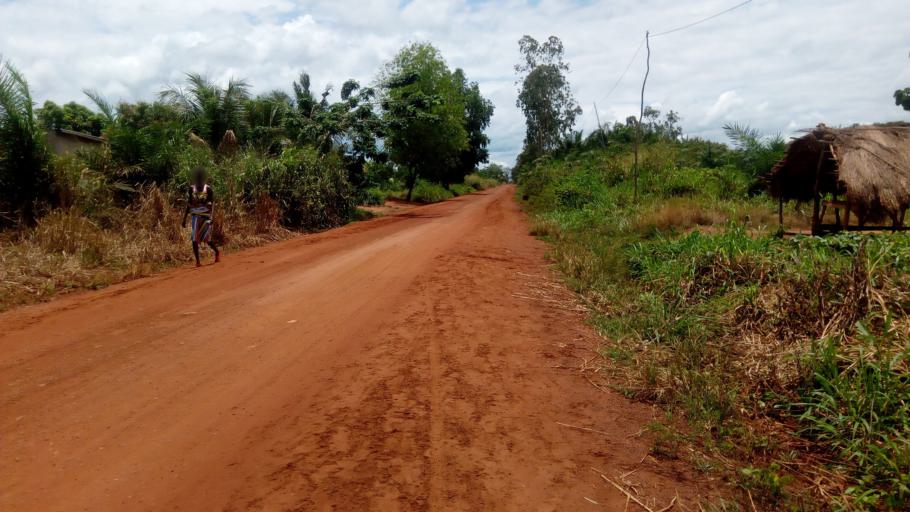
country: TG
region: Maritime
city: Tsevie
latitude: 6.3336
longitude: 1.0857
